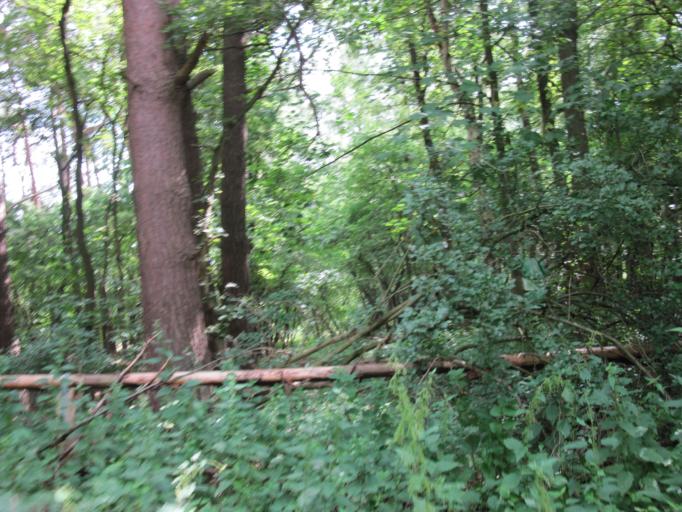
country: DE
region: North Rhine-Westphalia
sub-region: Regierungsbezirk Detmold
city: Paderborn
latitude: 51.7520
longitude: 8.7703
